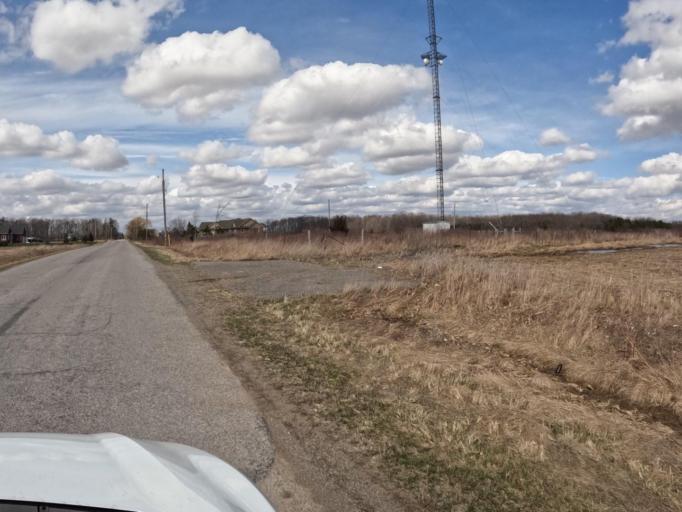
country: CA
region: Ontario
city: Norfolk County
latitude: 42.8685
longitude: -80.1931
